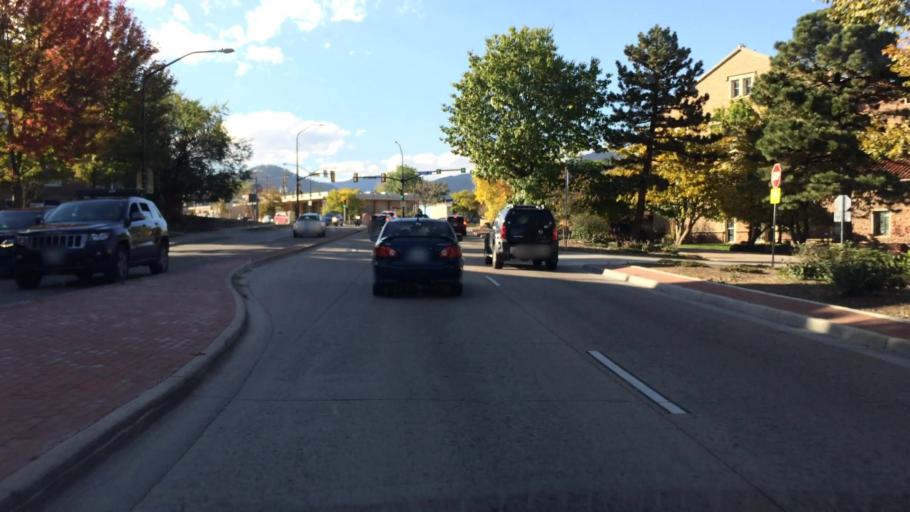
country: US
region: Colorado
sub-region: Boulder County
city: Boulder
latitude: 40.0067
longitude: -105.2737
